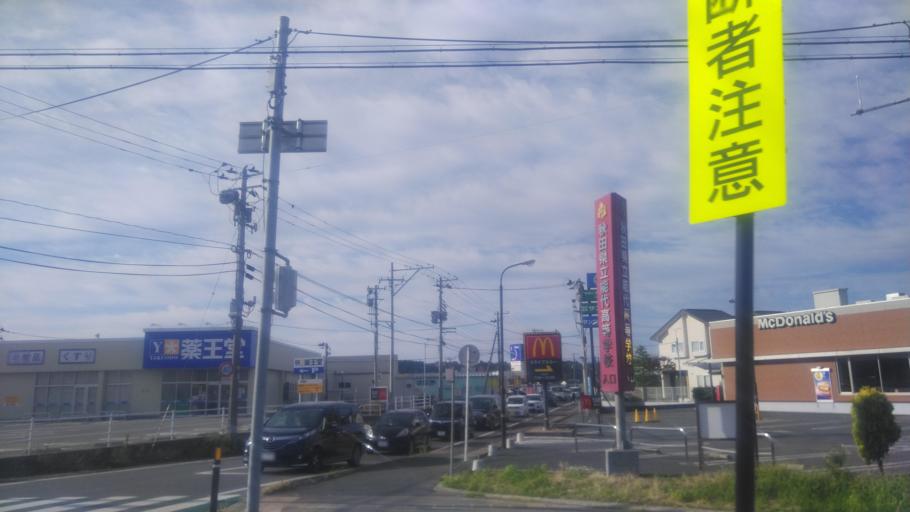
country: JP
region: Akita
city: Noshiromachi
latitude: 40.1848
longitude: 140.0519
